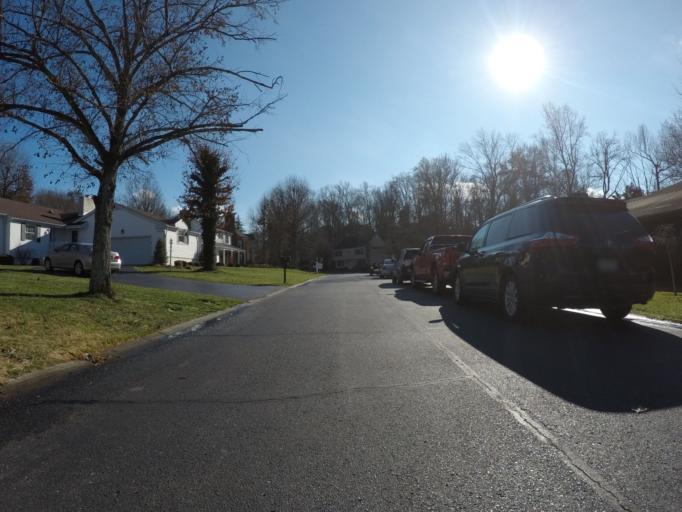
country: US
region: West Virginia
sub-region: Cabell County
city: Pea Ridge
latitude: 38.4165
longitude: -82.3264
